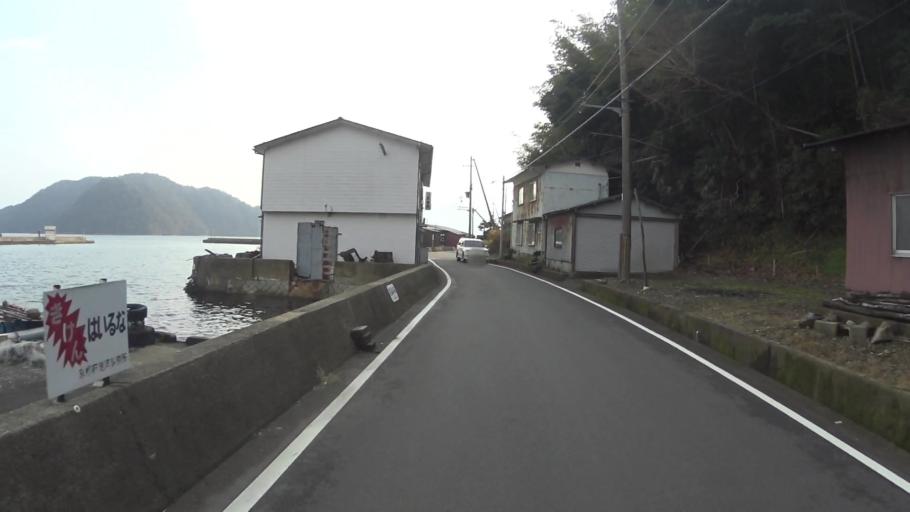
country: JP
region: Kyoto
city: Maizuru
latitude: 35.5033
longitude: 135.3329
